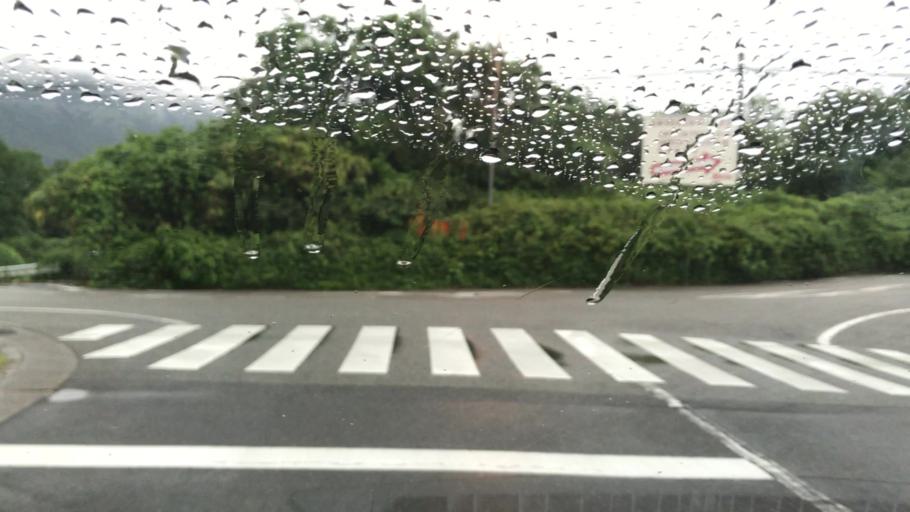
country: JP
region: Hyogo
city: Takarazuka
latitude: 34.8346
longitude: 135.2972
